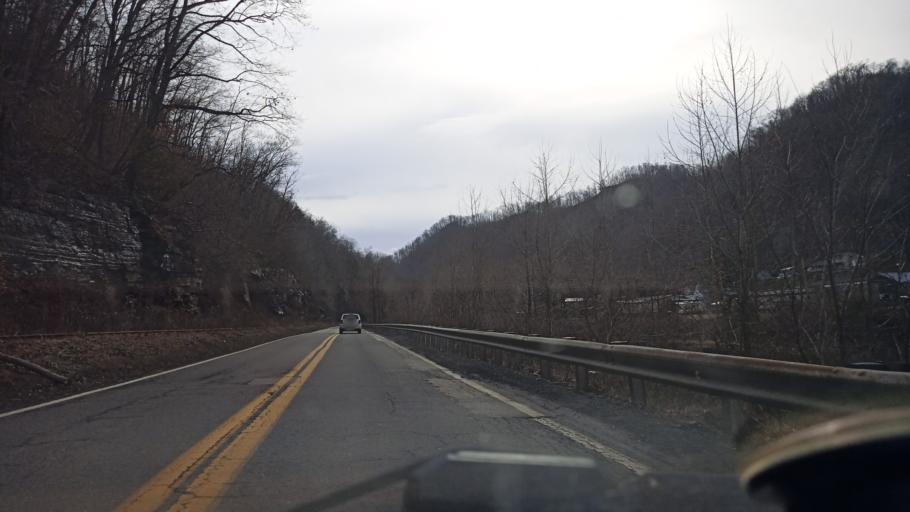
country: US
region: West Virginia
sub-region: Mingo County
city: Gilbert Creek
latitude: 37.6298
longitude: -81.8692
